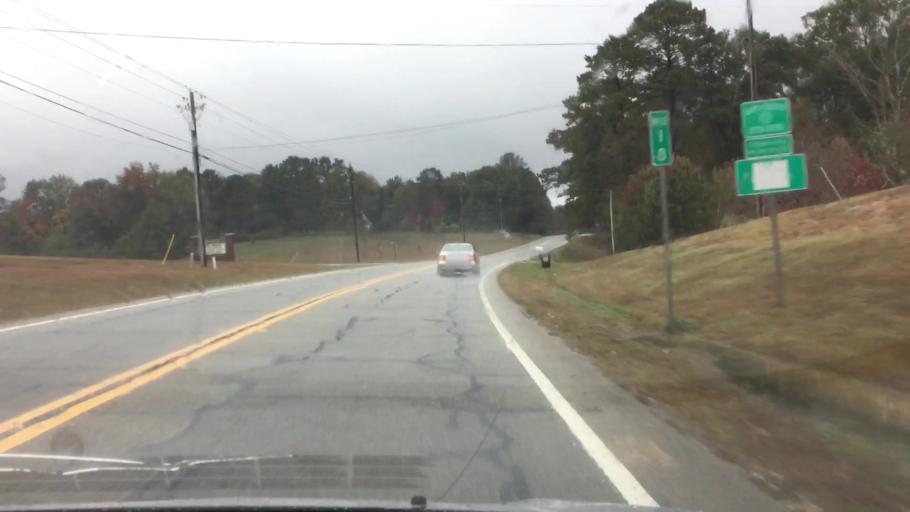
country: US
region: Georgia
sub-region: Henry County
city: Stockbridge
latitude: 33.5717
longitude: -84.1472
